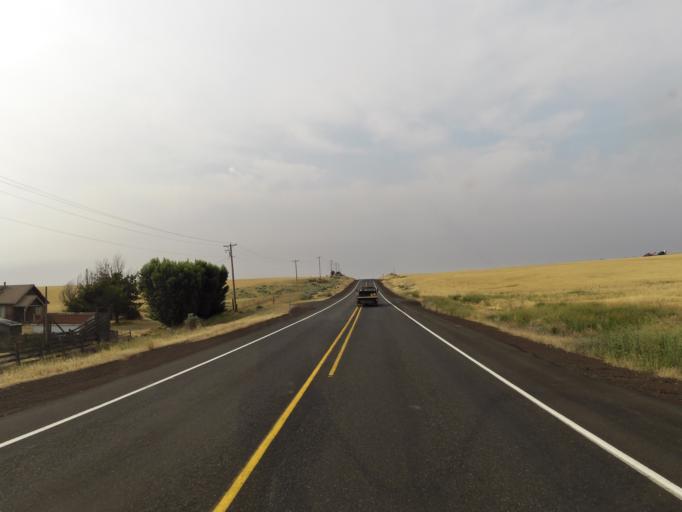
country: US
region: Oregon
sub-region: Sherman County
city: Moro
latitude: 45.4055
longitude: -120.7893
